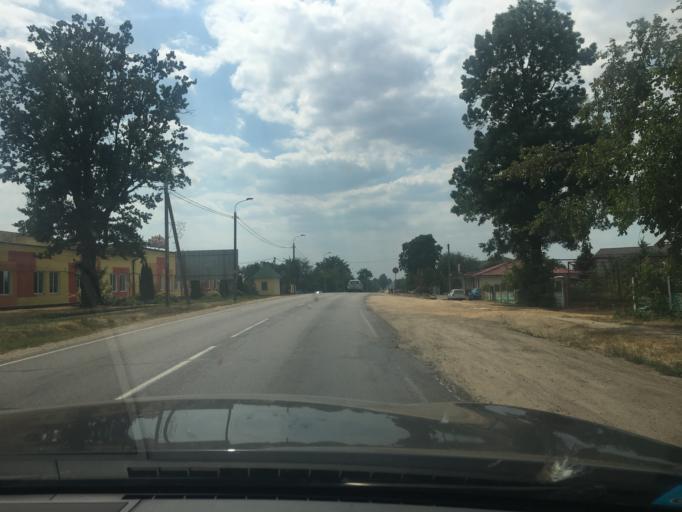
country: BY
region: Brest
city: Pruzhany
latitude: 52.5533
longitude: 24.4741
